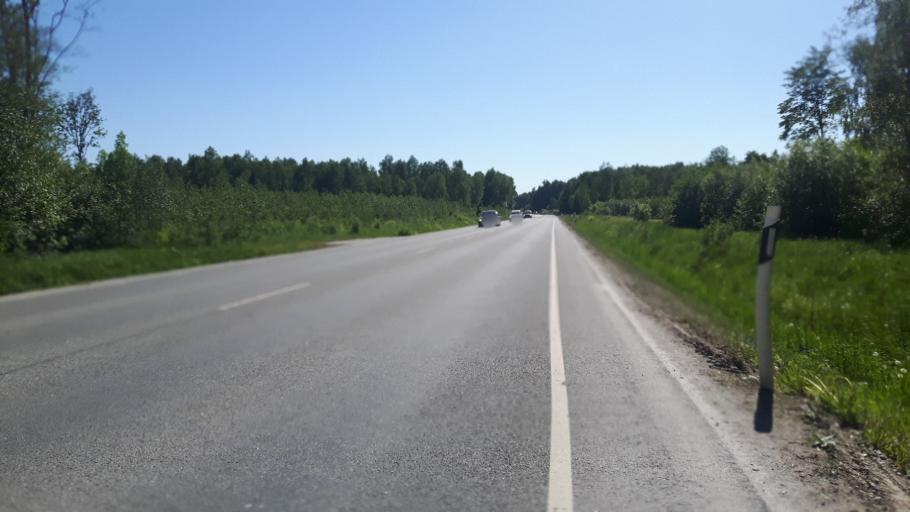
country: EE
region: Raplamaa
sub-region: Rapla vald
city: Rapla
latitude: 59.0278
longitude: 24.8180
